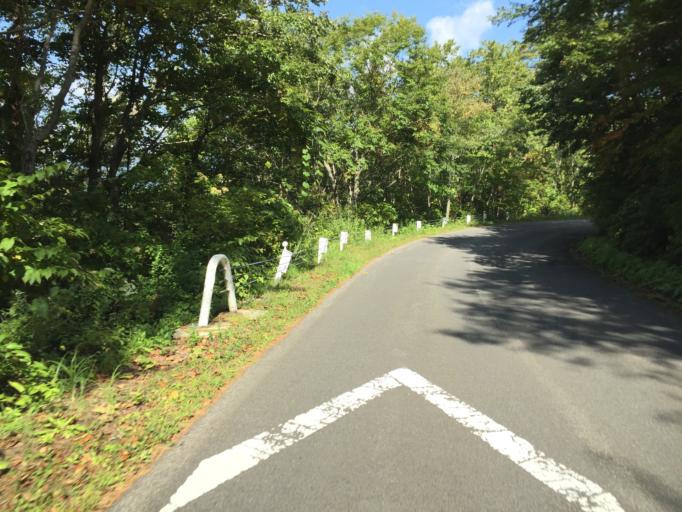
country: JP
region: Fukushima
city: Inawashiro
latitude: 37.6334
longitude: 140.0518
